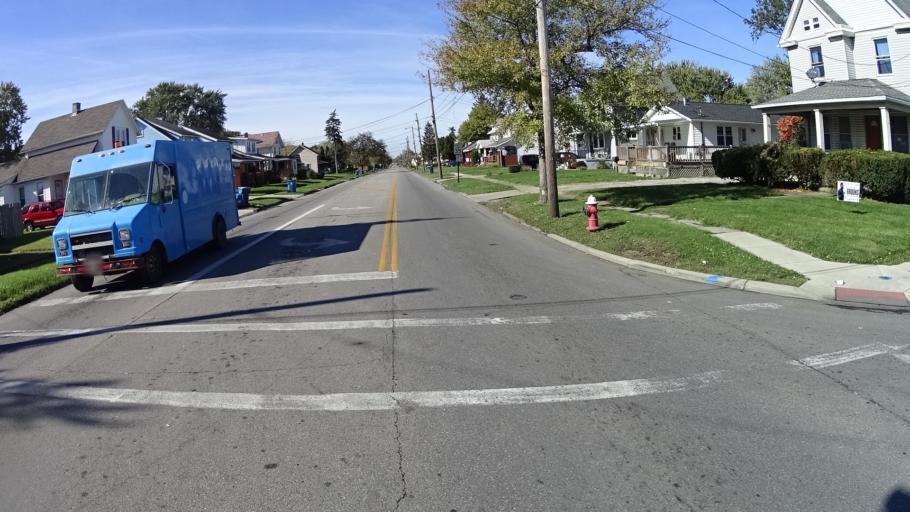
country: US
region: Ohio
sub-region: Lorain County
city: Lorain
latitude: 41.4509
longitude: -82.1792
